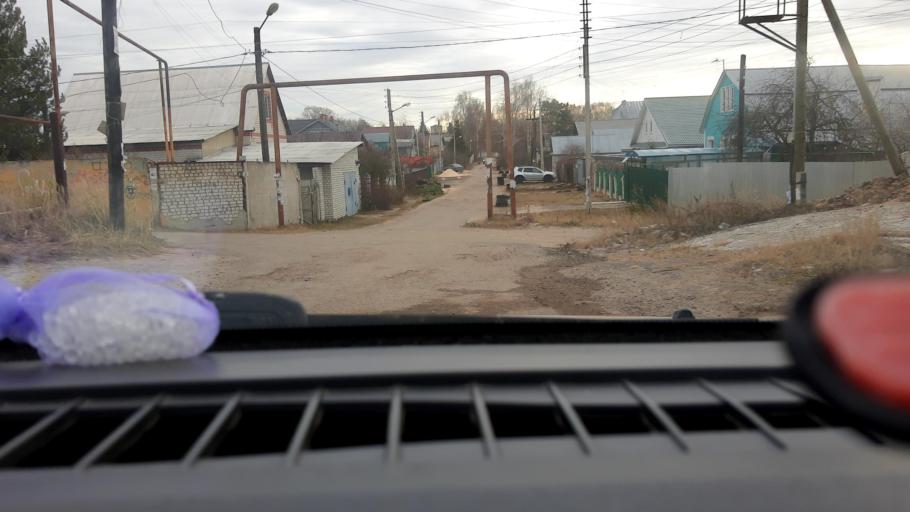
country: RU
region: Nizjnij Novgorod
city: Gorbatovka
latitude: 56.3842
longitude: 43.7747
